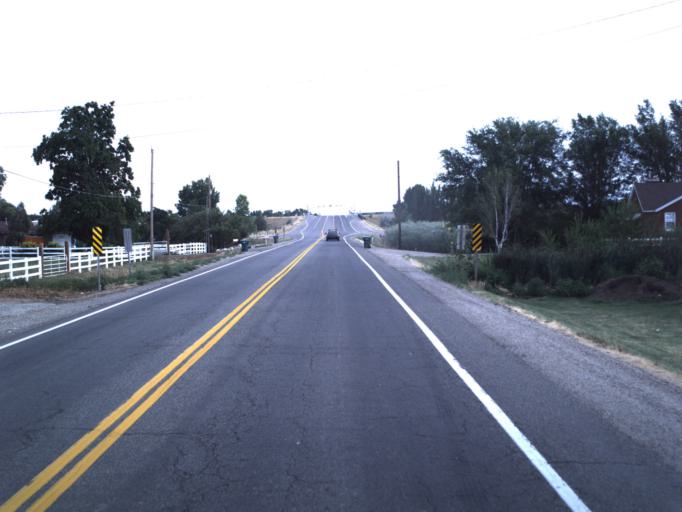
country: US
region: Utah
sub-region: Weber County
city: Marriott-Slaterville
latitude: 41.2504
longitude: -112.0253
